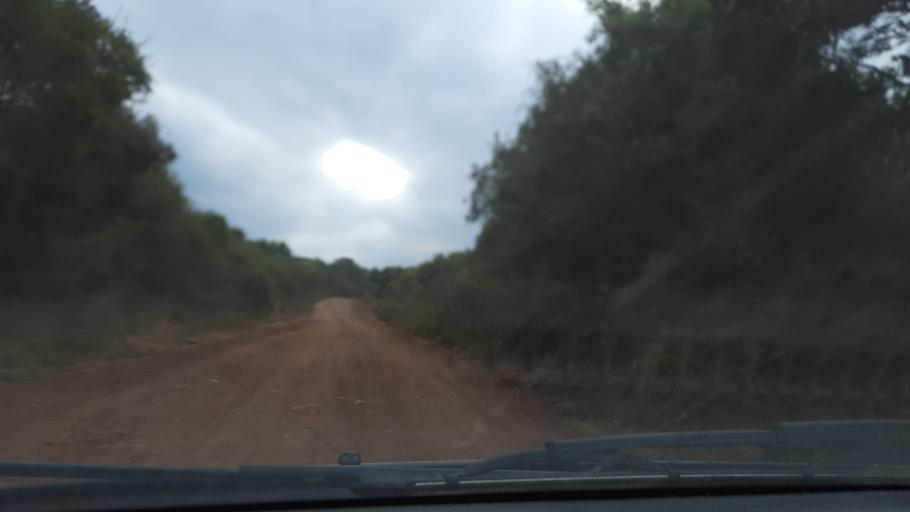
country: TZ
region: Kilimanjaro
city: Moshi
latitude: -2.8590
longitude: 37.2604
